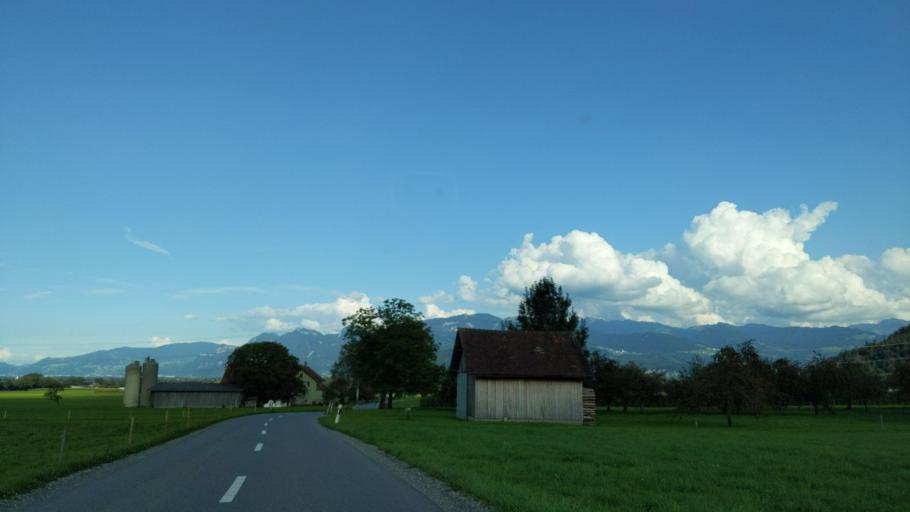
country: CH
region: Saint Gallen
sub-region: Wahlkreis Rheintal
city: Eichberg
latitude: 47.3359
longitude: 9.5355
